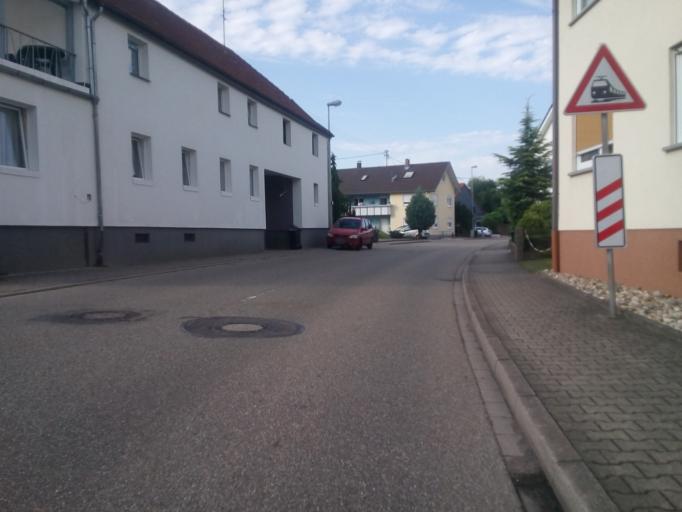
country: DE
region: Baden-Wuerttemberg
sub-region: Karlsruhe Region
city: Zell
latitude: 48.7188
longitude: 8.0664
